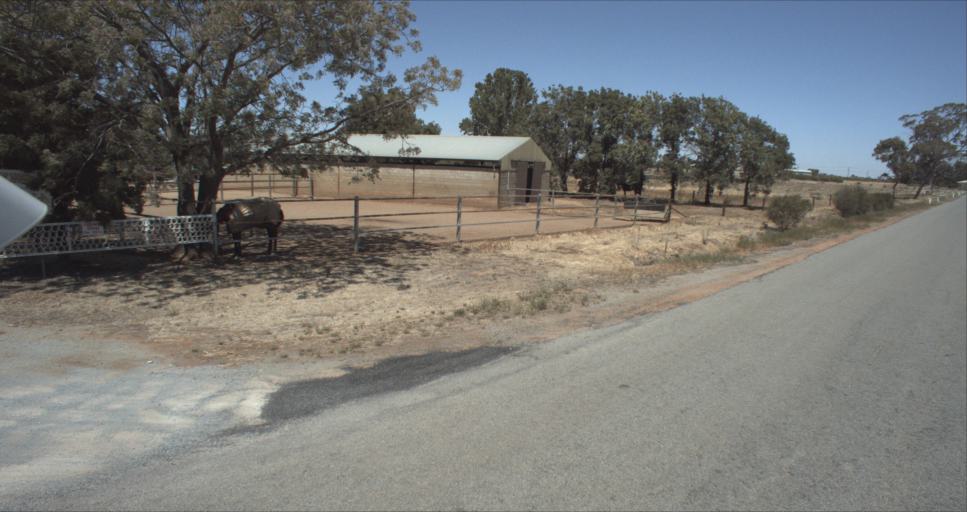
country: AU
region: New South Wales
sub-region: Leeton
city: Leeton
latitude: -34.5351
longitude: 146.3979
